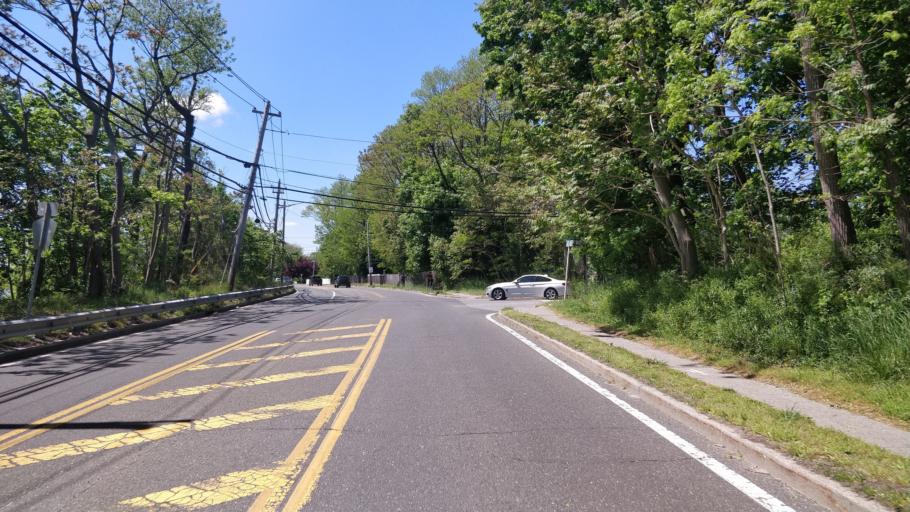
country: US
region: New York
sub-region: Suffolk County
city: Lake Ronkonkoma
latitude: 40.8304
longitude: -73.1171
